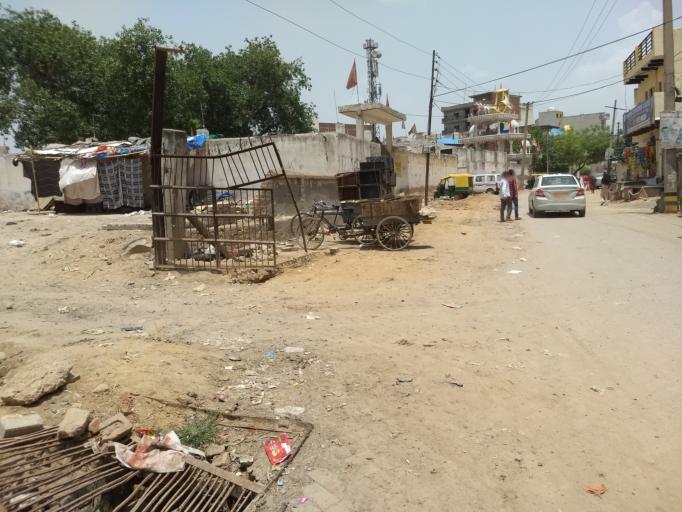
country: IN
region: Haryana
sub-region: Gurgaon
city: Gurgaon
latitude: 28.4887
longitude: 77.1024
